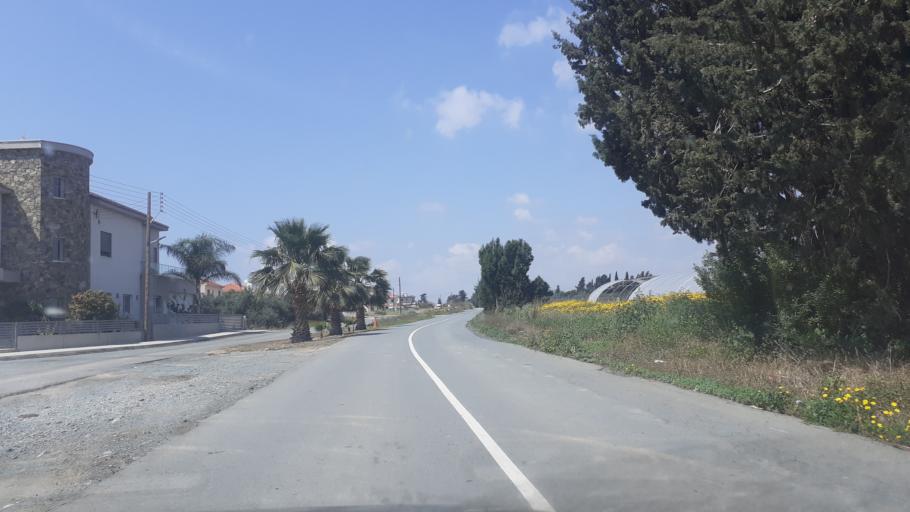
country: CY
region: Limassol
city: Ypsonas
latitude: 34.6628
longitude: 32.9603
